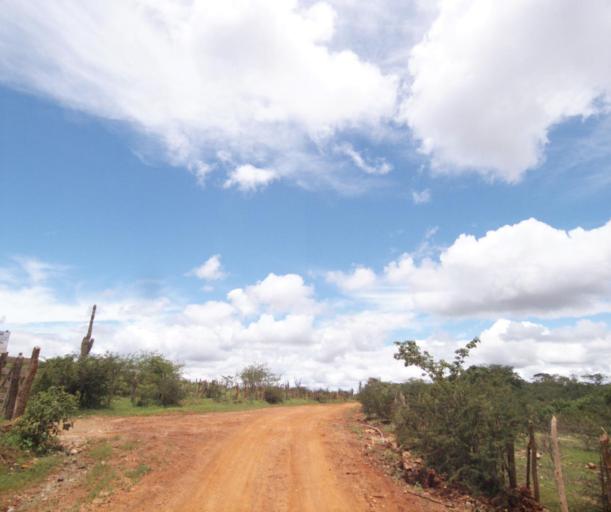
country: BR
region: Bahia
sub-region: Tanhacu
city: Tanhacu
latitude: -14.1904
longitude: -41.0785
